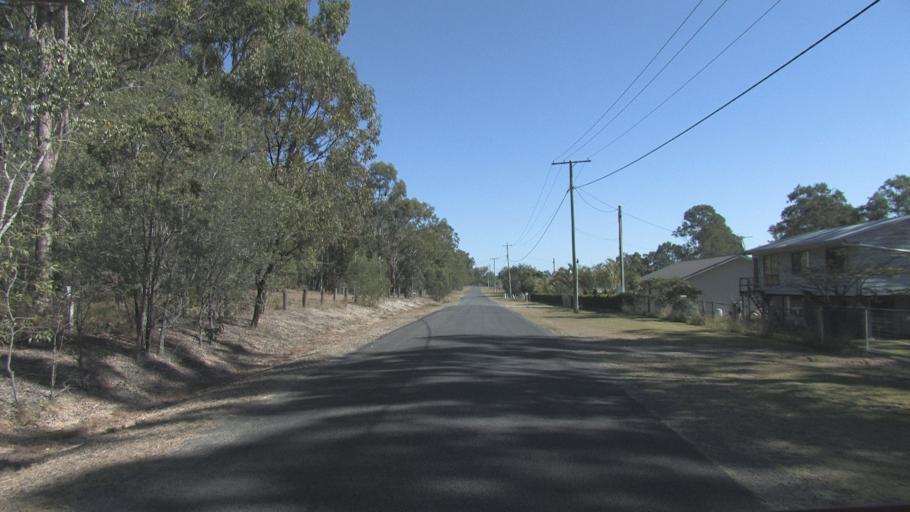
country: AU
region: Queensland
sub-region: Logan
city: Logan Reserve
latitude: -27.7580
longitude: 153.1274
